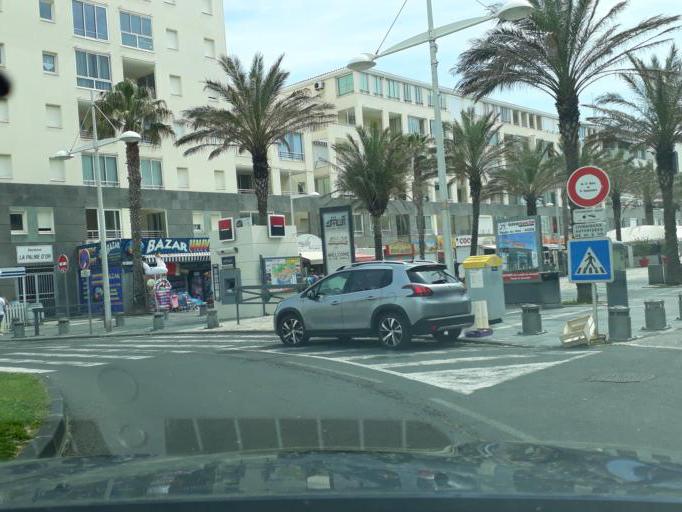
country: FR
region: Languedoc-Roussillon
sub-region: Departement de l'Herault
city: Le Cap d'Agde
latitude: 43.2762
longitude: 3.4841
